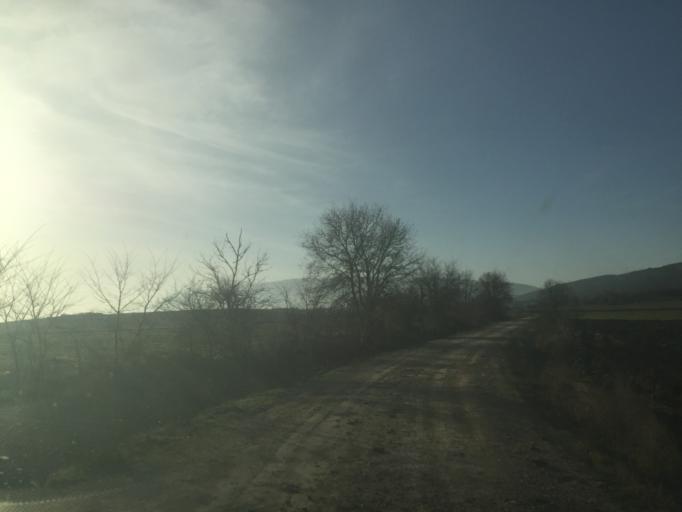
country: ES
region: Castille and Leon
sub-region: Provincia de Burgos
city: Medina de Pomar
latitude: 42.9383
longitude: -3.5946
